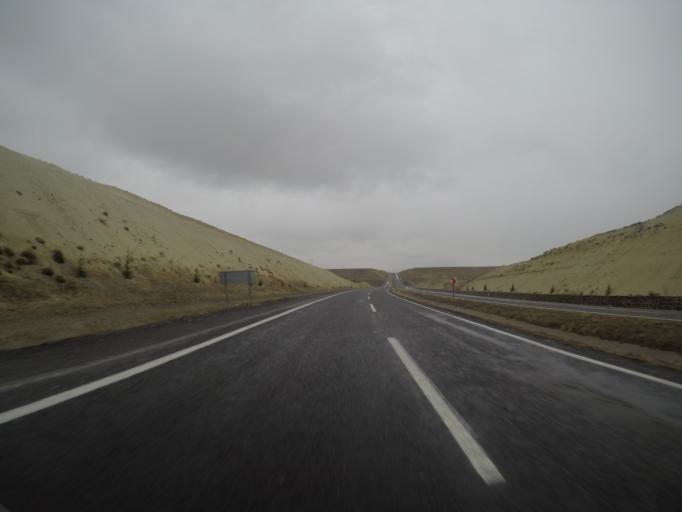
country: TR
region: Nevsehir
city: Urgub
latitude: 38.7423
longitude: 35.0055
